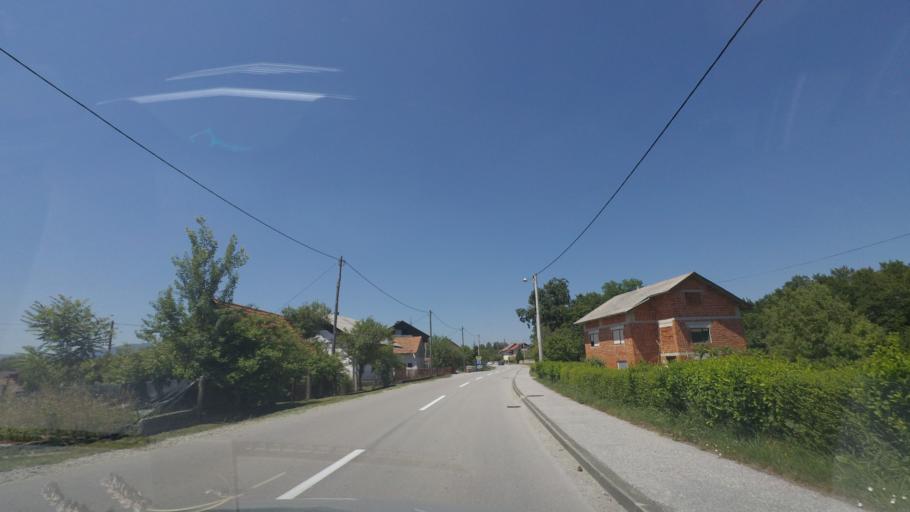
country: HR
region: Grad Zagreb
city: Horvati
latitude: 45.6866
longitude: 15.7466
